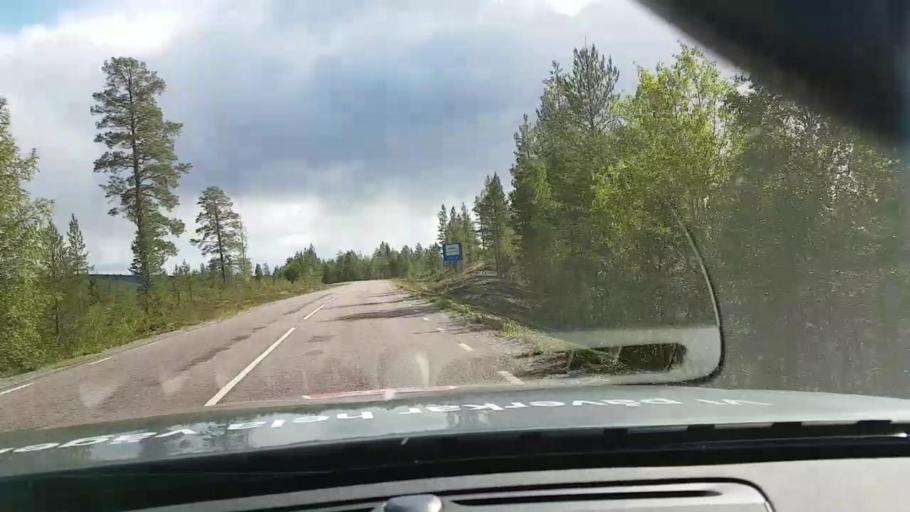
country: SE
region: Vaesterbotten
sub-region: Asele Kommun
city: Asele
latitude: 63.9048
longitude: 17.3441
